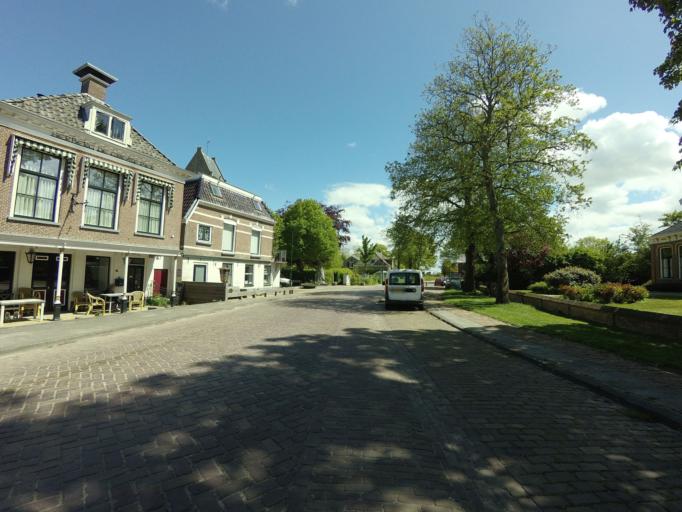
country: NL
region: Friesland
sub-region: Gemeente Harlingen
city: Harlingen
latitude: 53.1413
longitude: 5.4380
